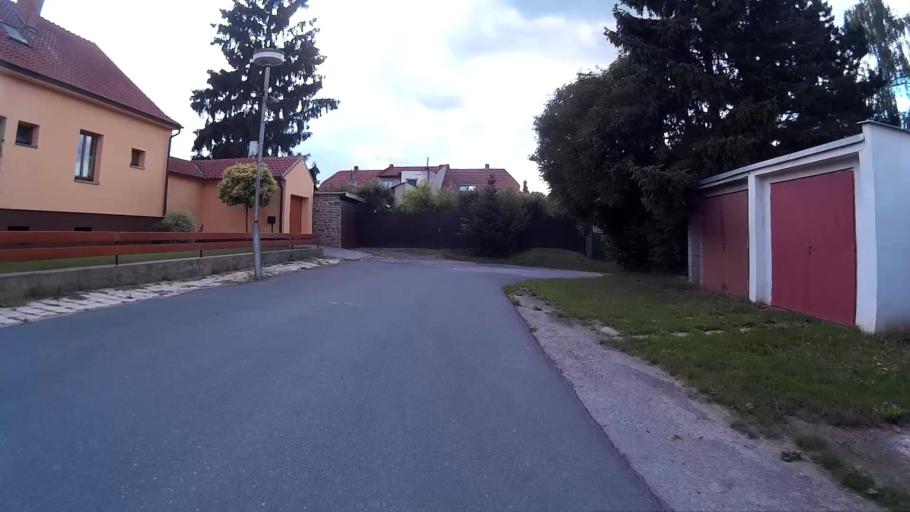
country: CZ
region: South Moravian
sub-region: Okres Brno-Venkov
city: Rosice
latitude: 49.1842
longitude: 16.3967
